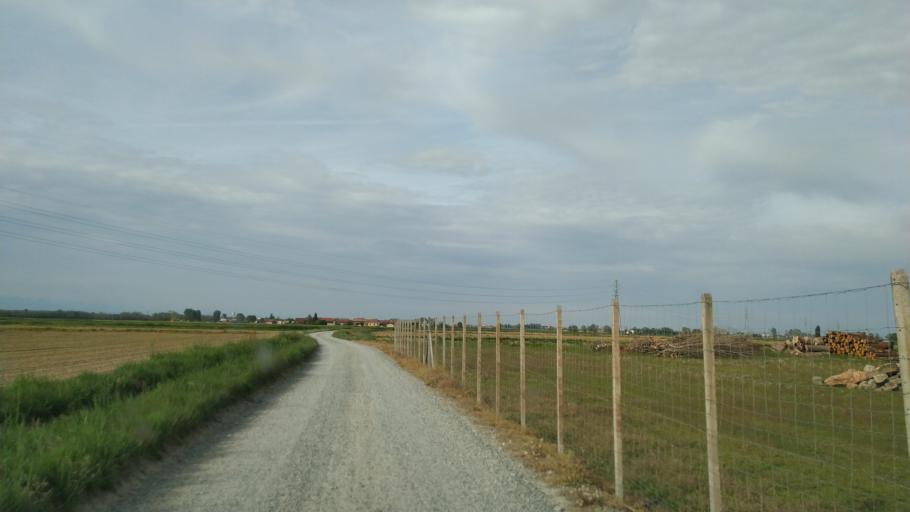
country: IT
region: Piedmont
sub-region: Provincia di Vercelli
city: Tronzano Vercellese
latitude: 45.3463
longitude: 8.1442
